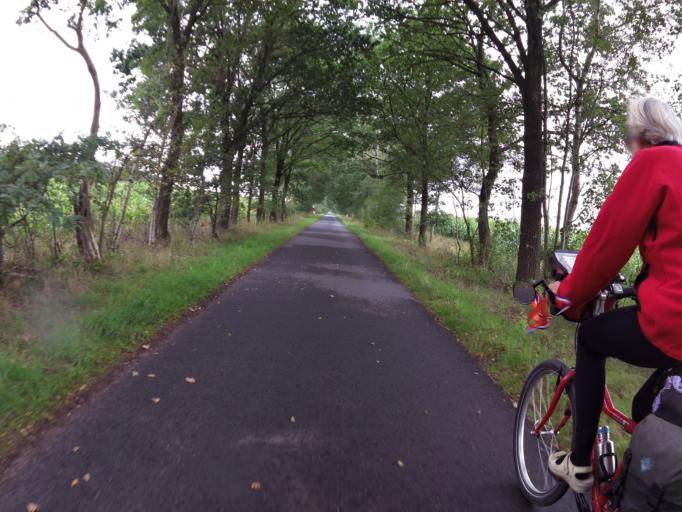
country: DE
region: Lower Saxony
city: Scheessel
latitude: 53.1451
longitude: 9.4446
